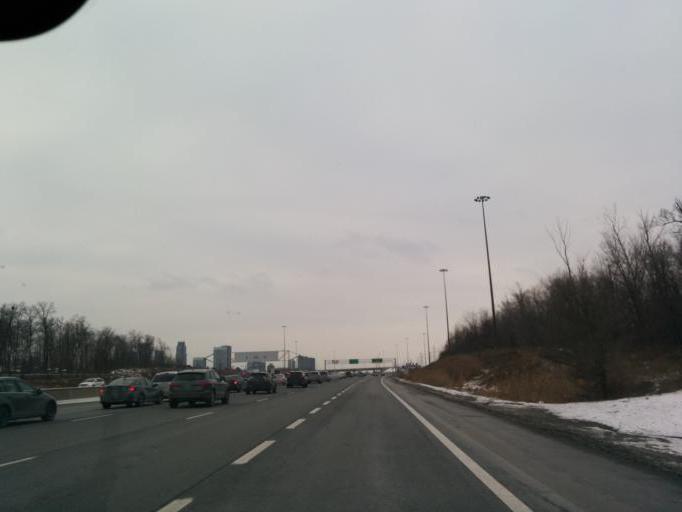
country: CA
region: Ontario
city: Mississauga
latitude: 43.6063
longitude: -79.6388
